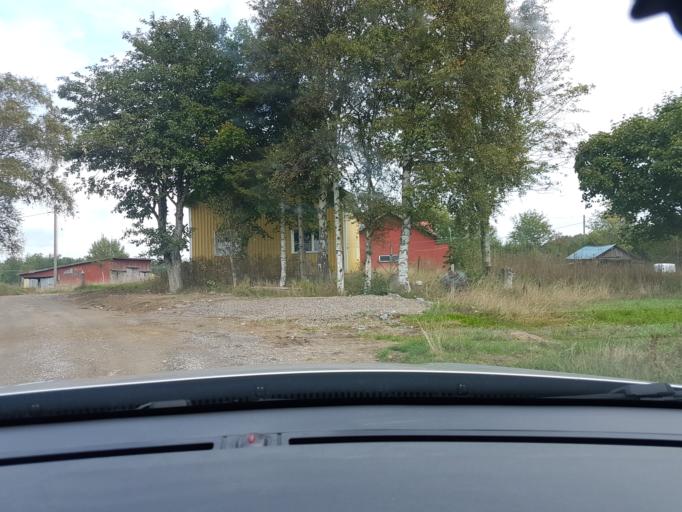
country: SE
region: Vaestra Goetaland
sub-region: Ale Kommun
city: Skepplanda
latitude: 57.8924
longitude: 12.2031
